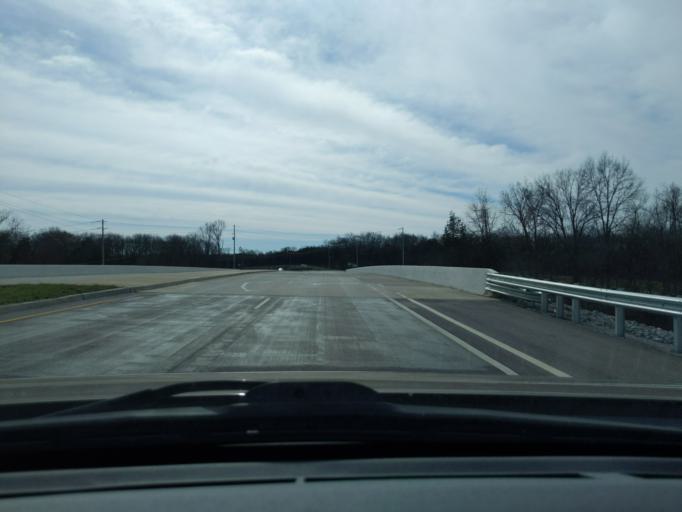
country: US
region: Tennessee
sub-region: Wilson County
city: Mount Juliet
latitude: 36.1950
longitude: -86.4794
